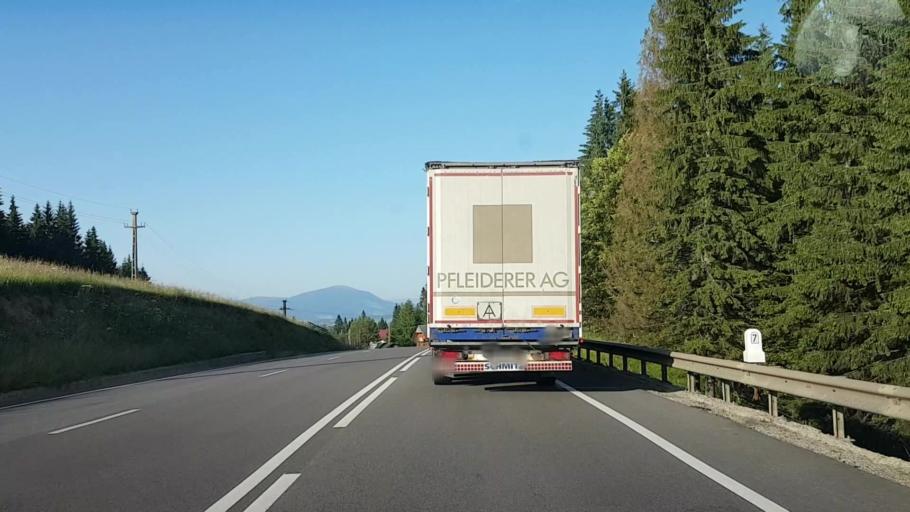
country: RO
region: Suceava
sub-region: Comuna Poiana Stampei
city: Poiana Stampei
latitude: 47.2866
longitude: 25.0718
